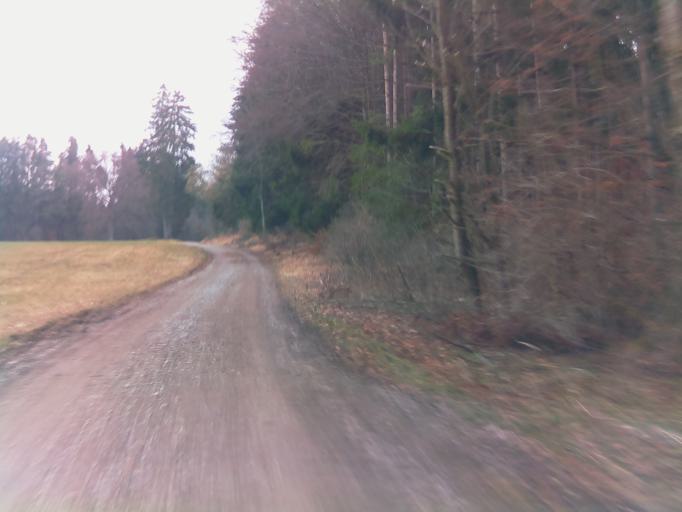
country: DE
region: Bavaria
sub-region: Upper Bavaria
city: Schwabsoien
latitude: 47.8446
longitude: 10.8051
